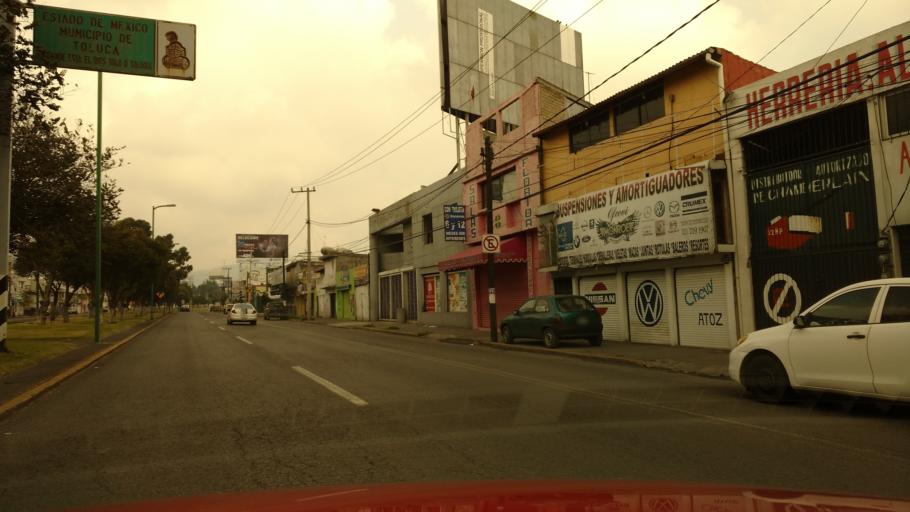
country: MX
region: Mexico
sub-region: Metepec
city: San Jorge Pueblo Nuevo
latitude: 19.2651
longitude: -99.6348
